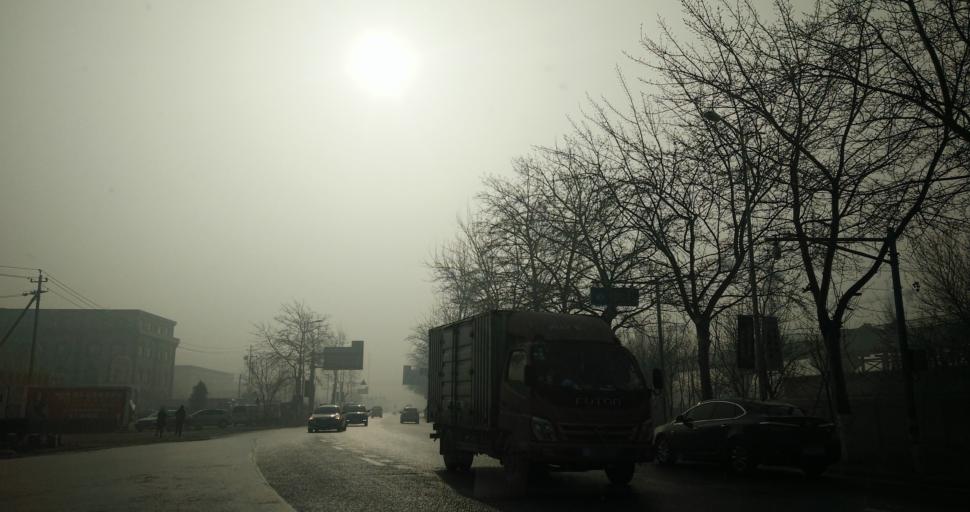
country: CN
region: Beijing
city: Yinghai
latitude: 39.7674
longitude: 116.4409
